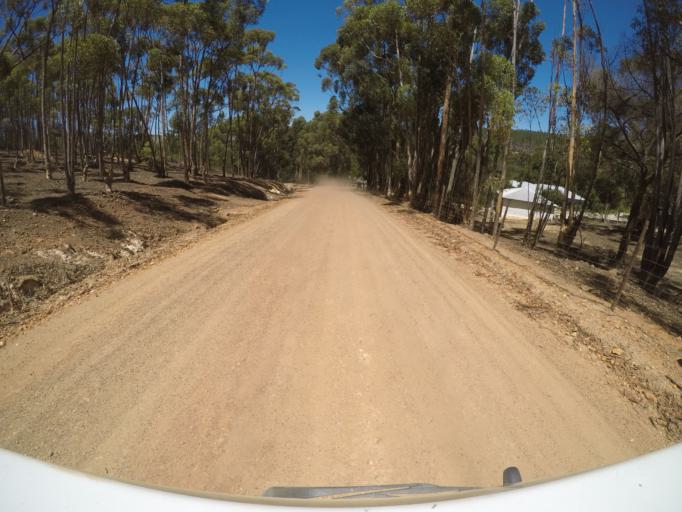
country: ZA
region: Western Cape
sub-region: Overberg District Municipality
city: Grabouw
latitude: -34.1678
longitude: 19.2247
